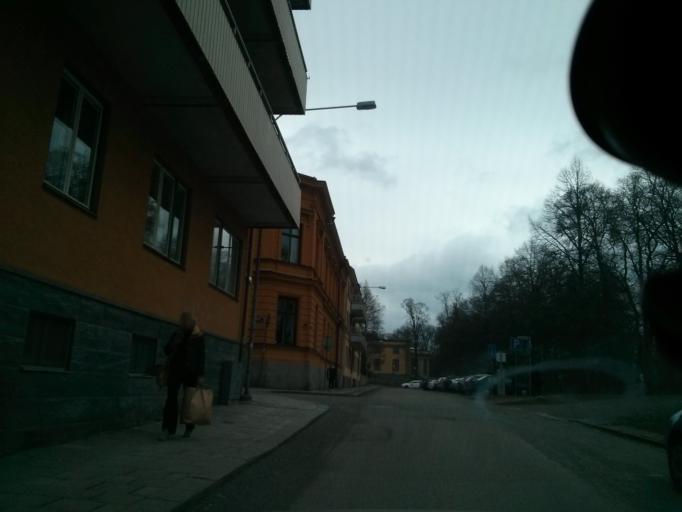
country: SE
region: Uppsala
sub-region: Uppsala Kommun
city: Uppsala
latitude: 59.8561
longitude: 17.6283
